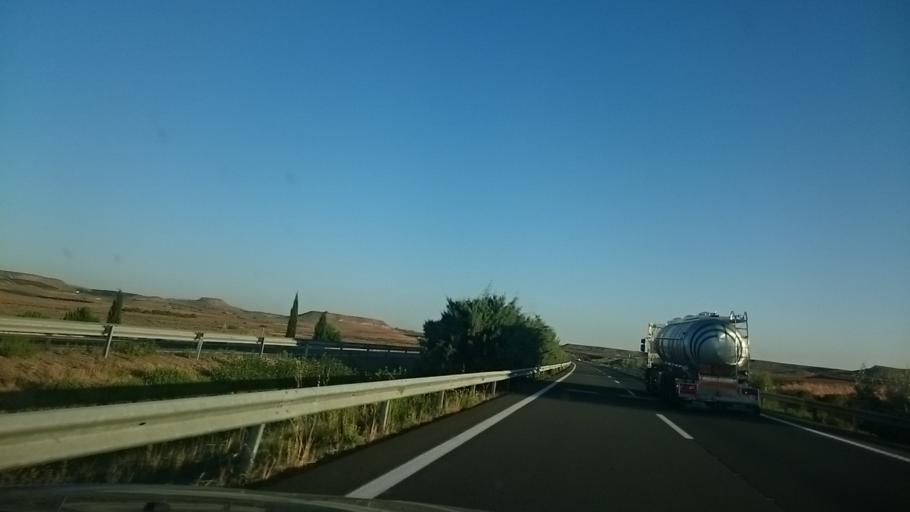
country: ES
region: La Rioja
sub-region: Provincia de La Rioja
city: Rincon de Soto
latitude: 42.1912
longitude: -1.8444
